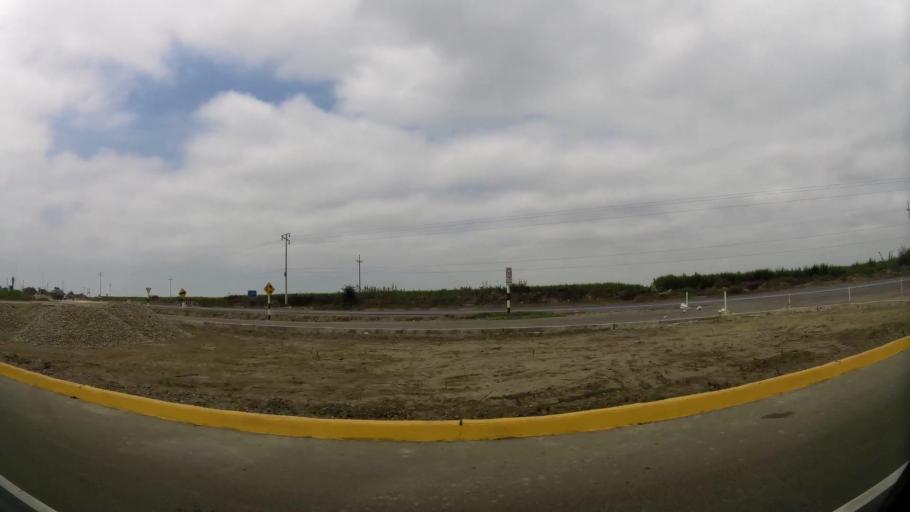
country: PE
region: La Libertad
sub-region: Ascope
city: Chocope
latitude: -7.7890
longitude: -79.2325
